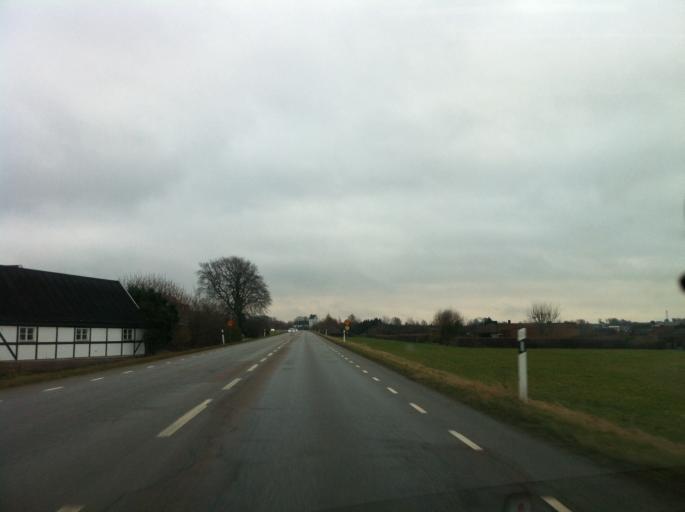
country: SE
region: Skane
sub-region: Helsingborg
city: Glumslov
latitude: 55.9513
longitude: 12.7994
